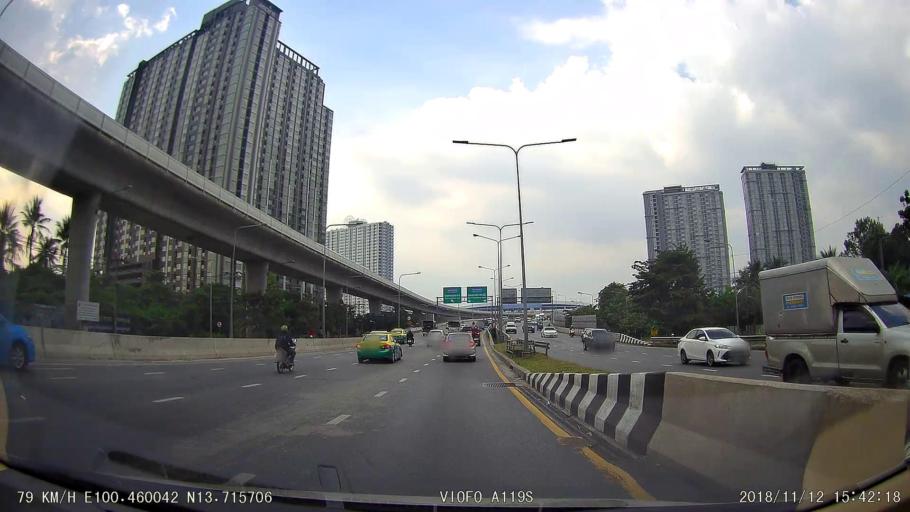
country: TH
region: Bangkok
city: Bangkok Yai
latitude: 13.7159
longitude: 100.4599
